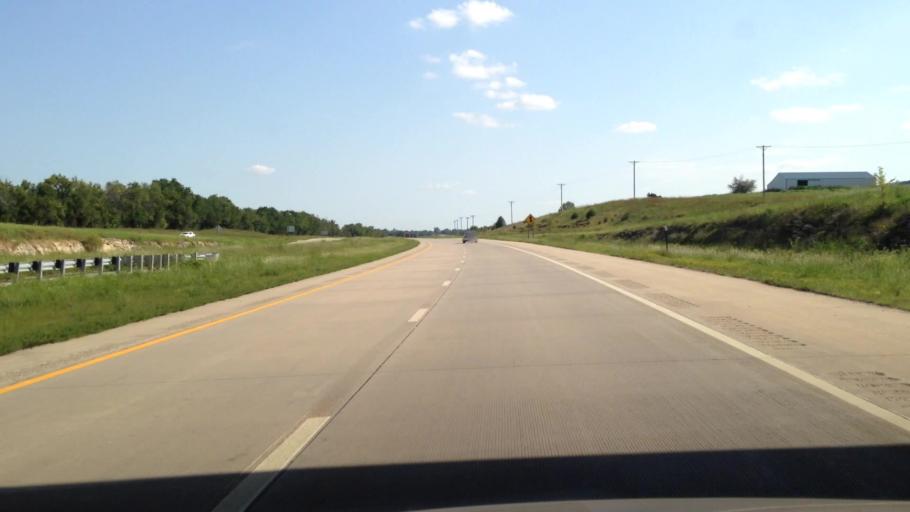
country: US
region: Kansas
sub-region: Bourbon County
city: Fort Scott
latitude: 37.8922
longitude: -94.7056
